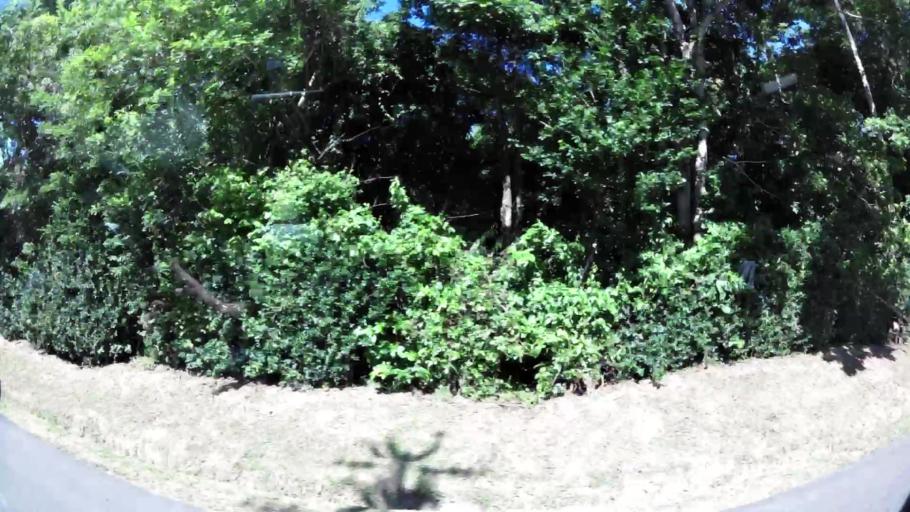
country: TT
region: Tobago
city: Scarborough
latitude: 11.1780
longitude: -60.7142
